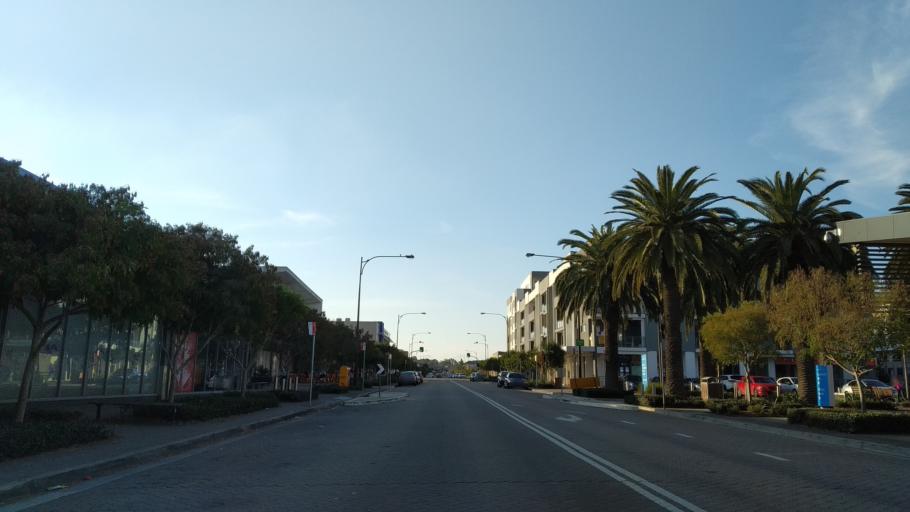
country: AU
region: New South Wales
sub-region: Penrith Municipality
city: Werrington Downs
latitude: -33.7277
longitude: 150.7258
